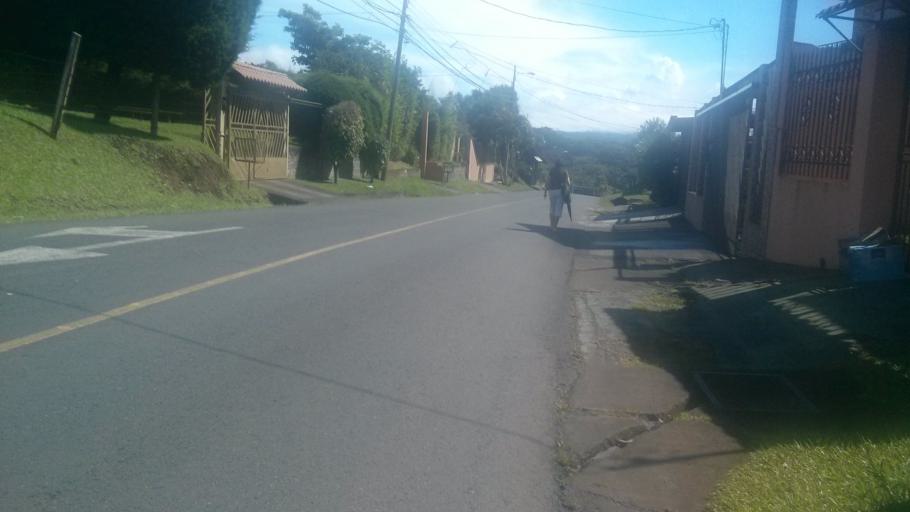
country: CR
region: Heredia
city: Angeles
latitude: 10.0212
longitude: -84.0503
